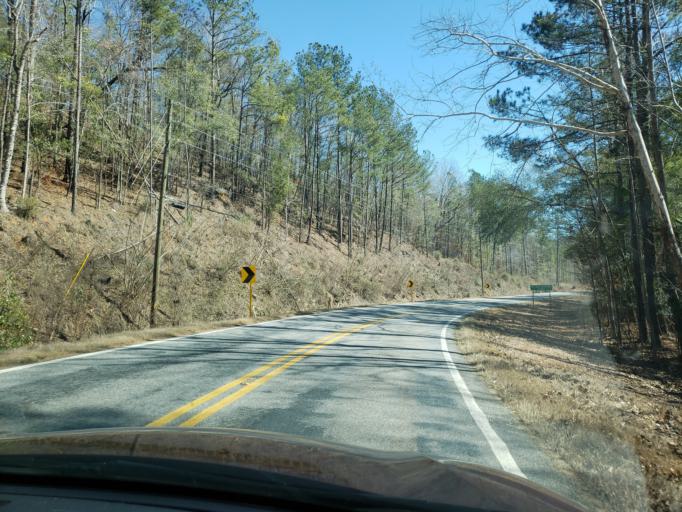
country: US
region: Alabama
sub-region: Elmore County
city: Eclectic
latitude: 32.6770
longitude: -85.9074
